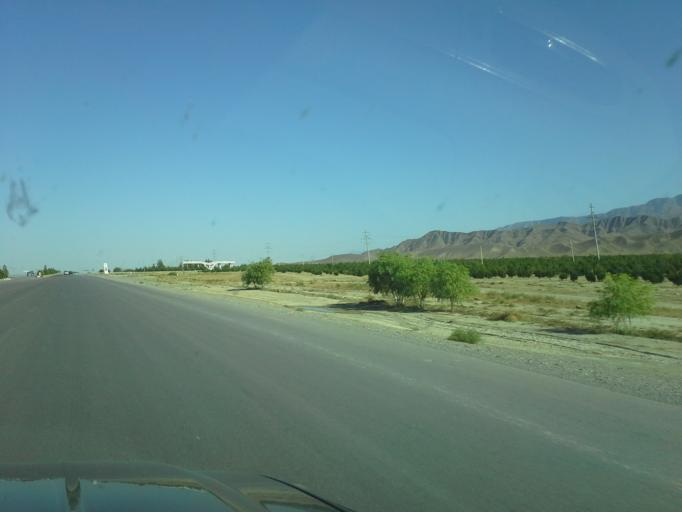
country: TM
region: Ahal
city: Baharly
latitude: 38.2771
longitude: 57.6815
